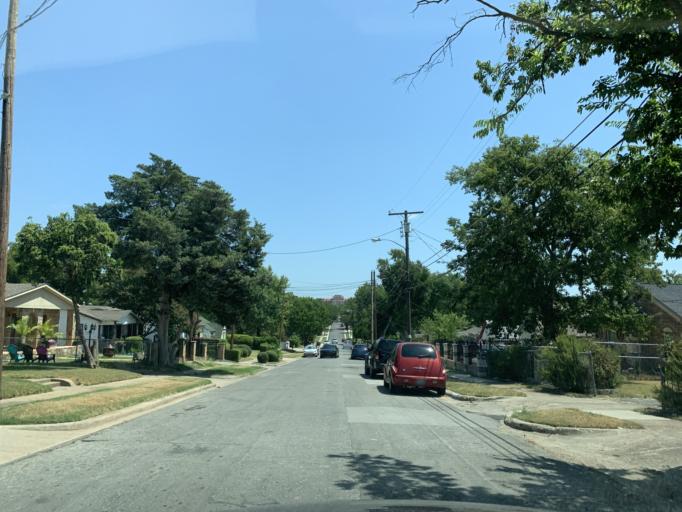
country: US
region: Texas
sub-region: Dallas County
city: Dallas
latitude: 32.6925
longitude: -96.7985
